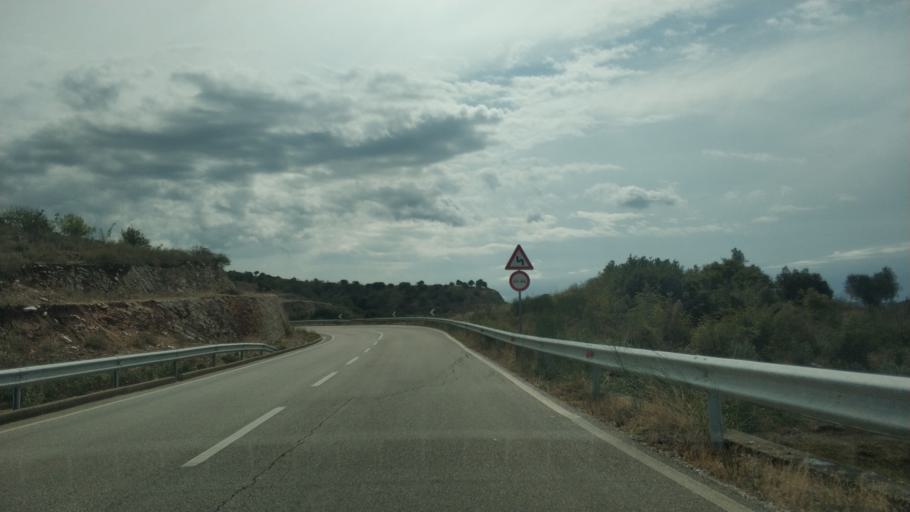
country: AL
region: Vlore
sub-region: Rrethi i Sarandes
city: Xarre
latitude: 39.7521
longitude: 20.0037
